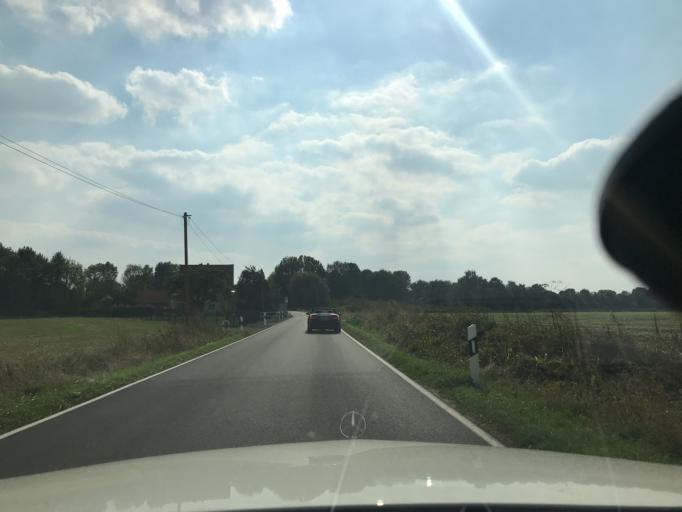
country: DE
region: North Rhine-Westphalia
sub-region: Regierungsbezirk Arnsberg
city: Werl
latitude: 51.5979
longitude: 7.8755
